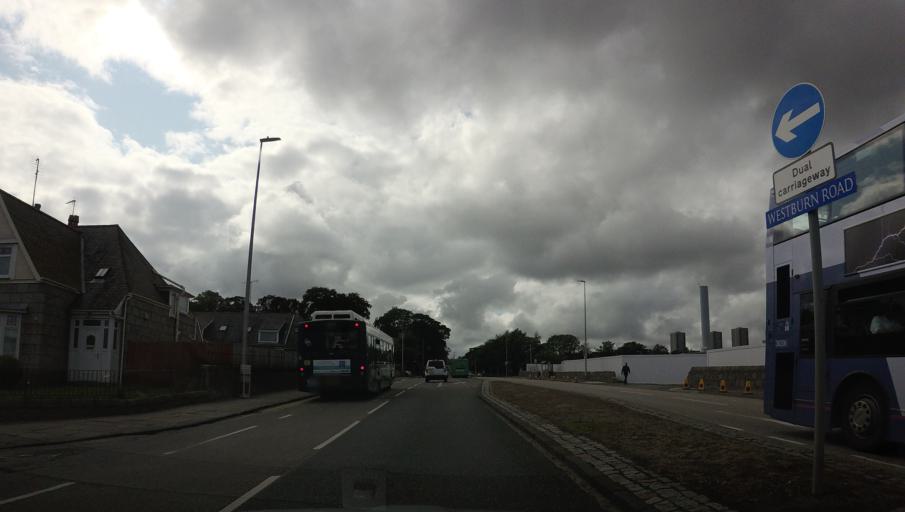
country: GB
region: Scotland
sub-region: Aberdeen City
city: Aberdeen
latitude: 57.1520
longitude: -2.1357
